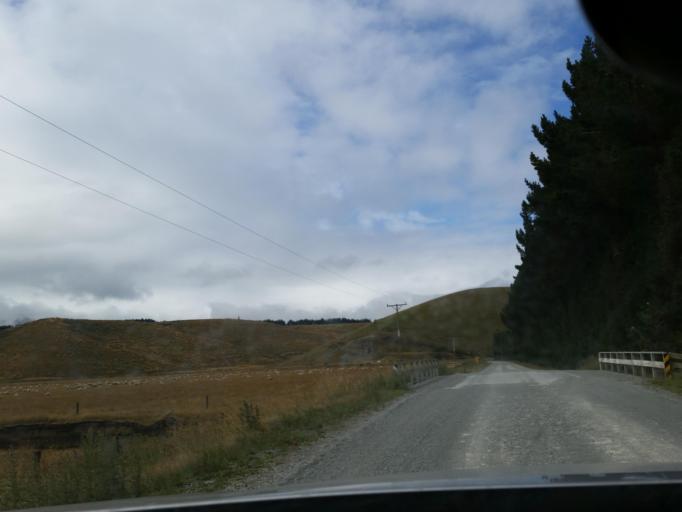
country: NZ
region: Southland
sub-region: Southland District
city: Te Anau
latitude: -45.4544
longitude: 168.0785
